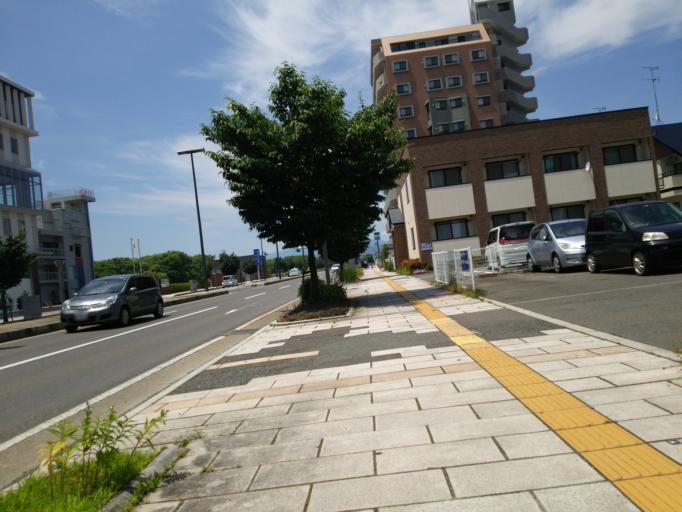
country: JP
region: Iwate
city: Morioka-shi
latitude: 39.7009
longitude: 141.1300
